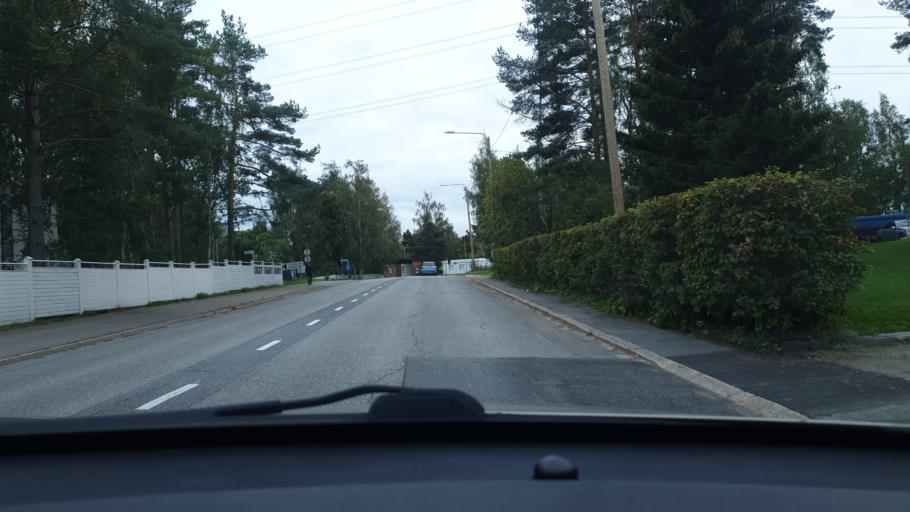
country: FI
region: Ostrobothnia
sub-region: Vaasa
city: Korsholm
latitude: 63.0978
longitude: 21.6687
